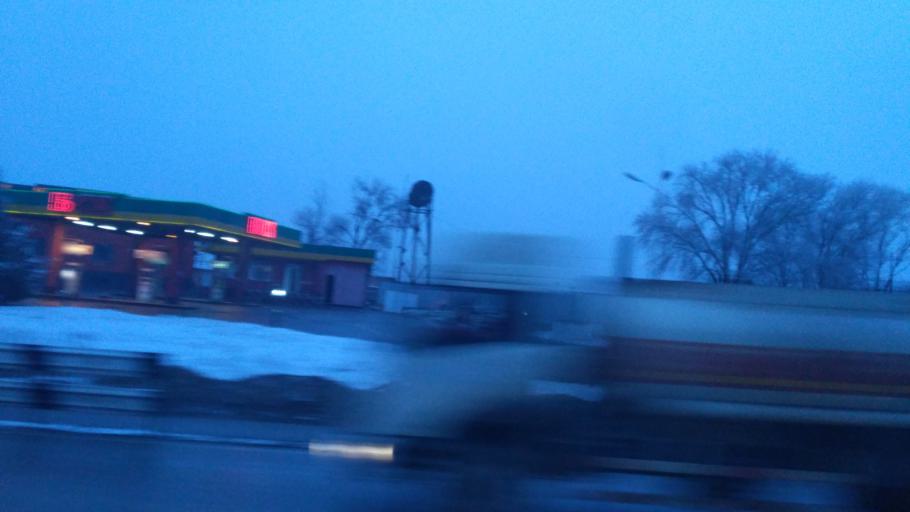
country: KZ
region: Ongtustik Qazaqstan
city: Shymkent
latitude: 42.3630
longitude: 69.5188
